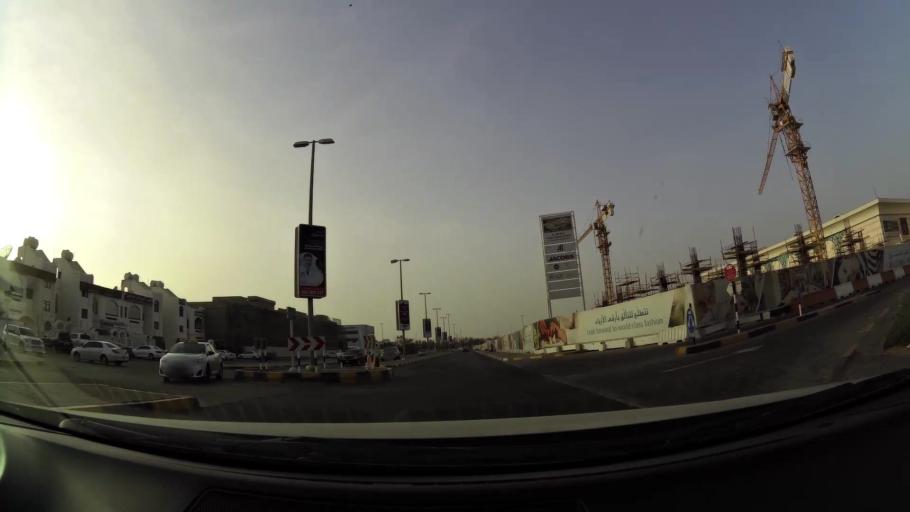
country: AE
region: Abu Dhabi
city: Al Ain
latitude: 24.2435
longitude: 55.7250
